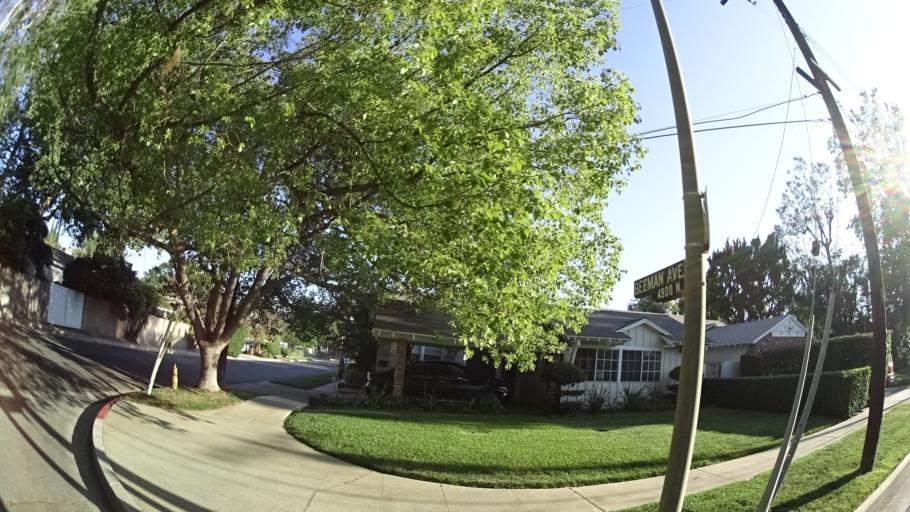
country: US
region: California
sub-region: Los Angeles County
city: North Hollywood
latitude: 34.1603
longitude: -118.4078
